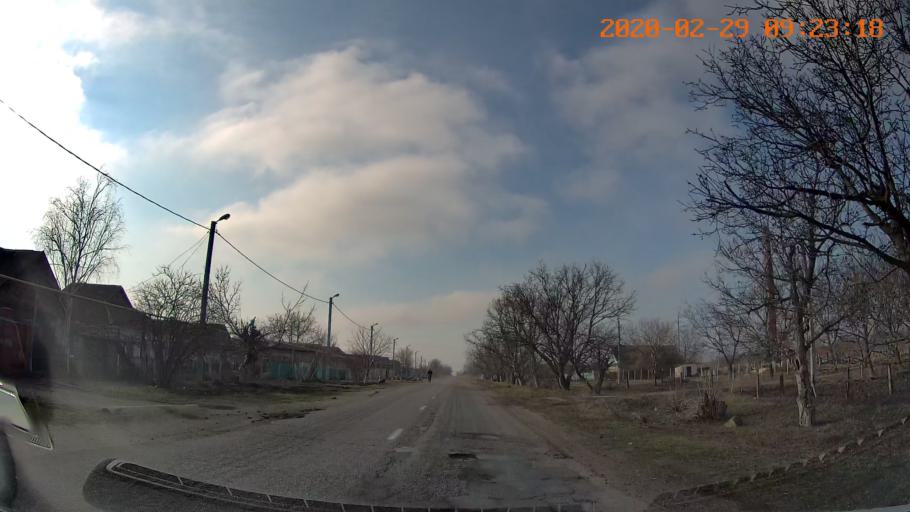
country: MD
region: Telenesti
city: Pervomaisc
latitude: 46.7272
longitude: 29.9616
